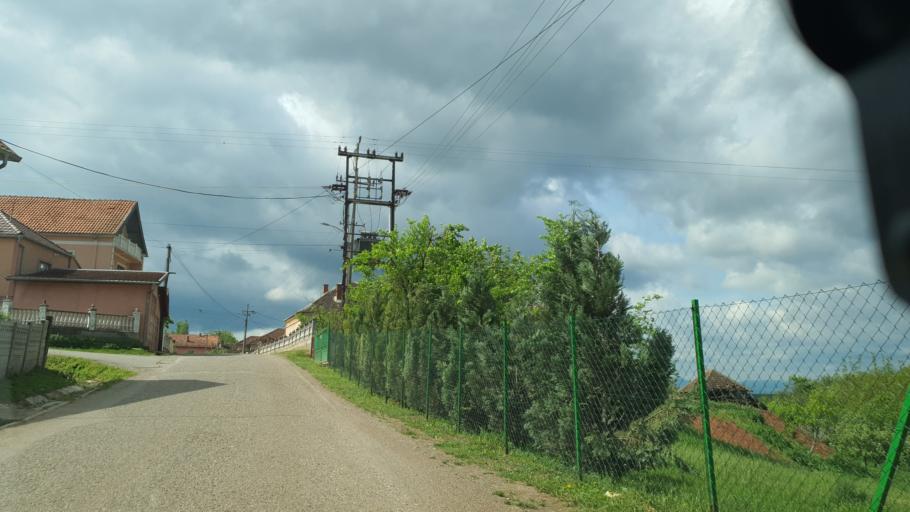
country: RS
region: Central Serbia
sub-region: Pomoravski Okrug
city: Paracin
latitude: 43.9450
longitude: 21.4945
